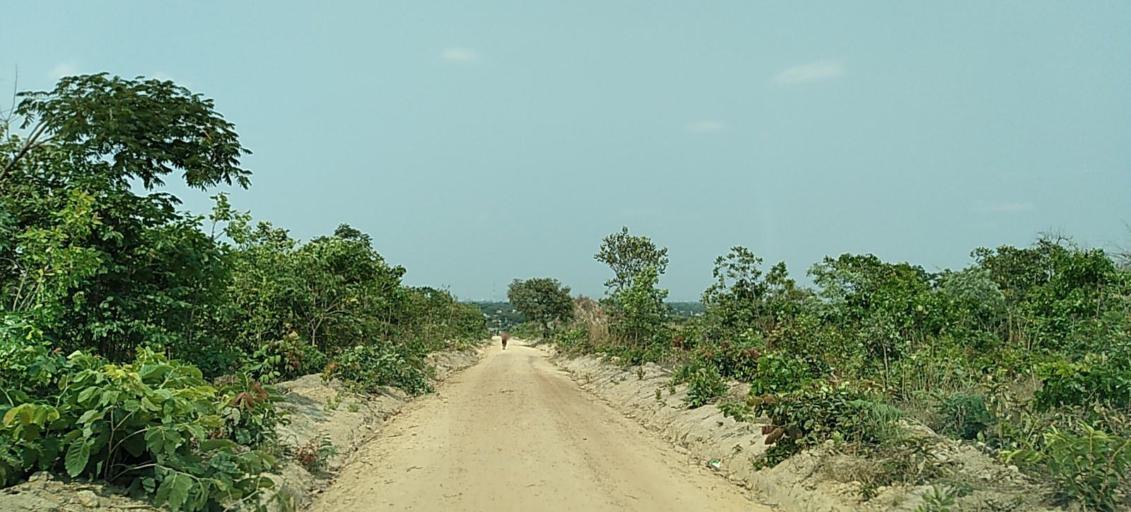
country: ZM
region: Copperbelt
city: Chambishi
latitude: -12.6228
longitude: 28.0850
